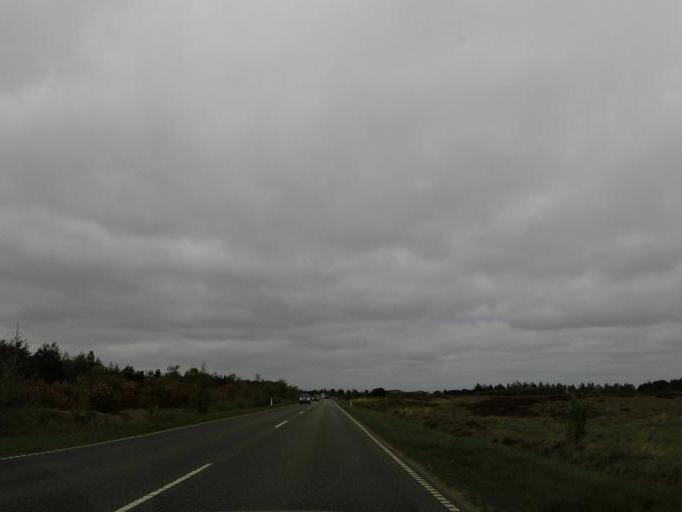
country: DE
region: Schleswig-Holstein
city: List
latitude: 55.1153
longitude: 8.5448
